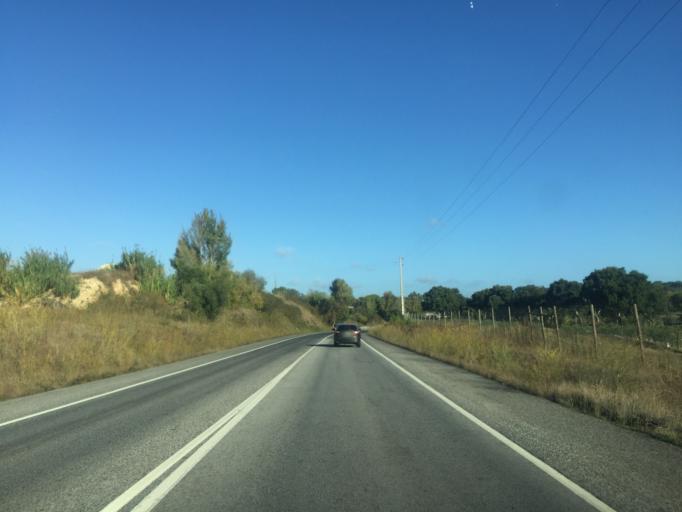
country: PT
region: Lisbon
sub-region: Azambuja
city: Alcoentre
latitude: 39.2057
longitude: -8.9546
